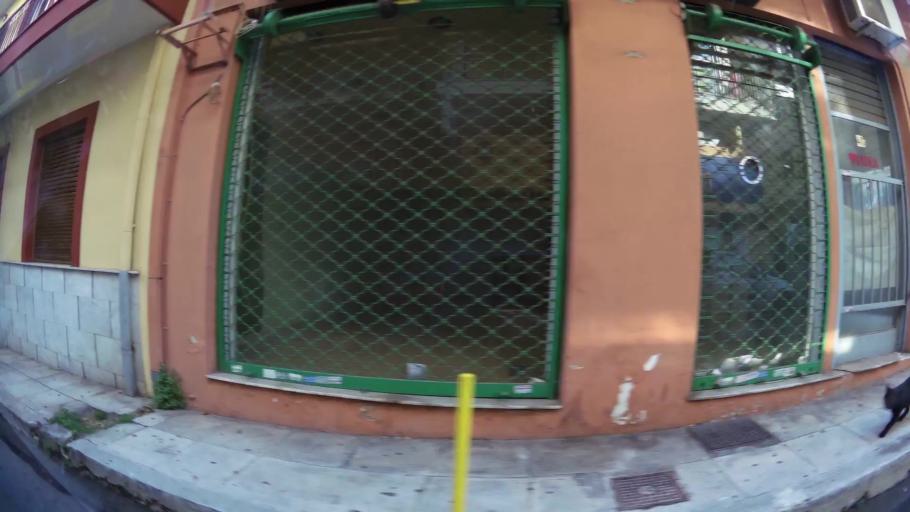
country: GR
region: Attica
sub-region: Nomarchia Athinas
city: Kaisariani
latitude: 37.9760
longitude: 23.7686
